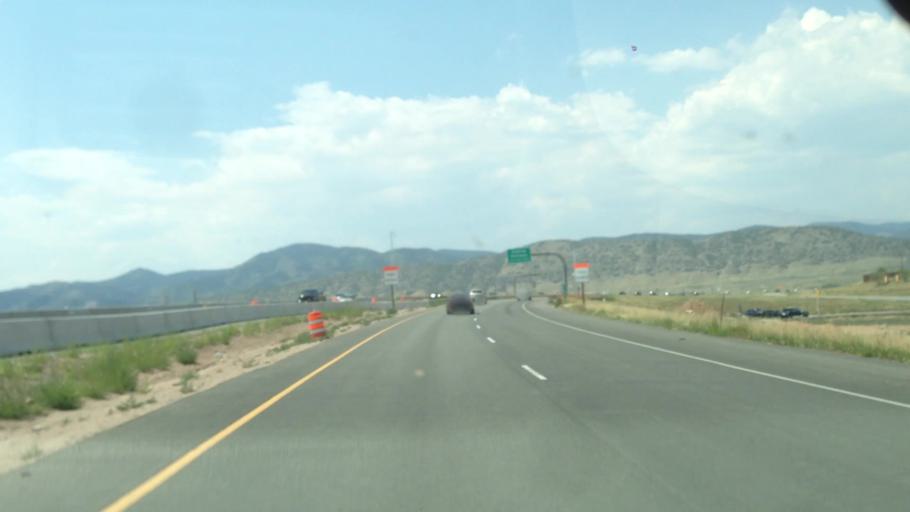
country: US
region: Colorado
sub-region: Jefferson County
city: Columbine
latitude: 39.5553
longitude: -105.0829
